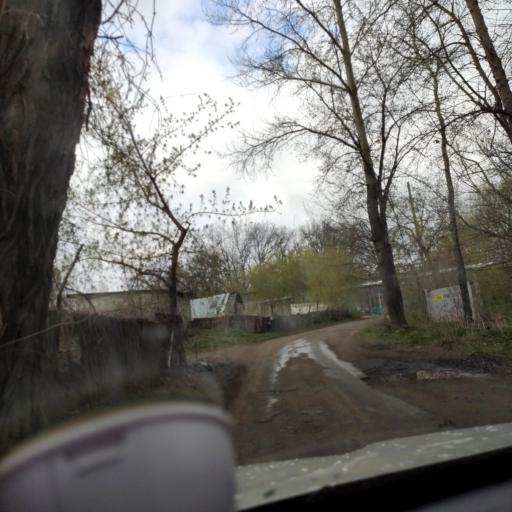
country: RU
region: Samara
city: Novokuybyshevsk
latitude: 53.1412
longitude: 49.9699
